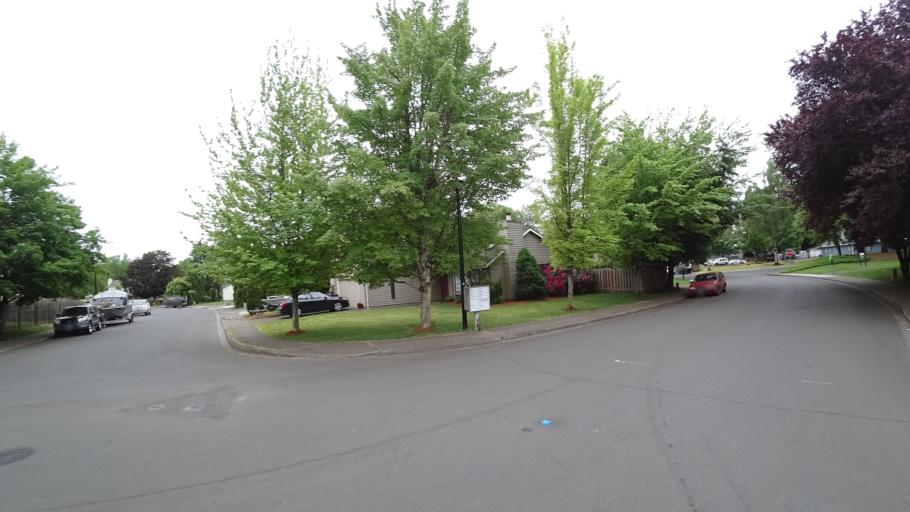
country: US
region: Oregon
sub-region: Washington County
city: Rockcreek
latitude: 45.5610
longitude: -122.8961
